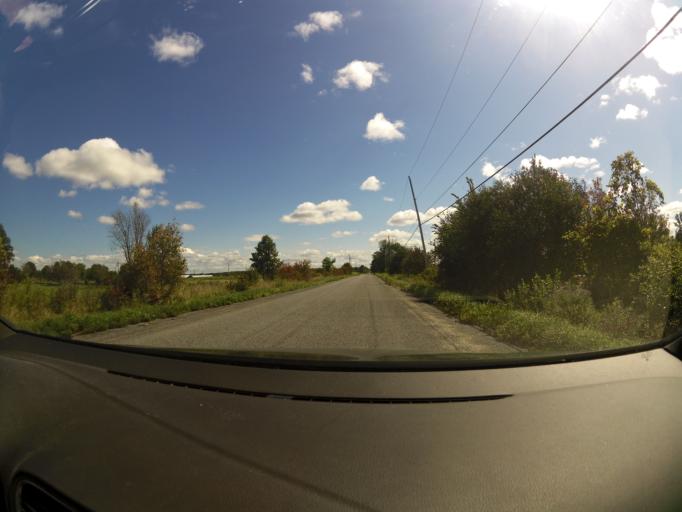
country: CA
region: Ontario
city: Carleton Place
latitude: 45.2262
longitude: -76.1426
